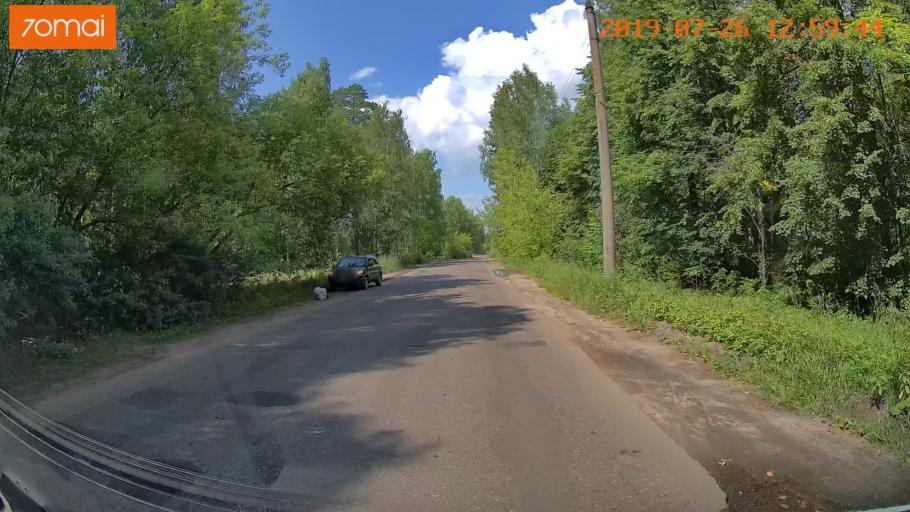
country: RU
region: Ivanovo
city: Bogorodskoye
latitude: 57.0302
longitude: 41.0201
